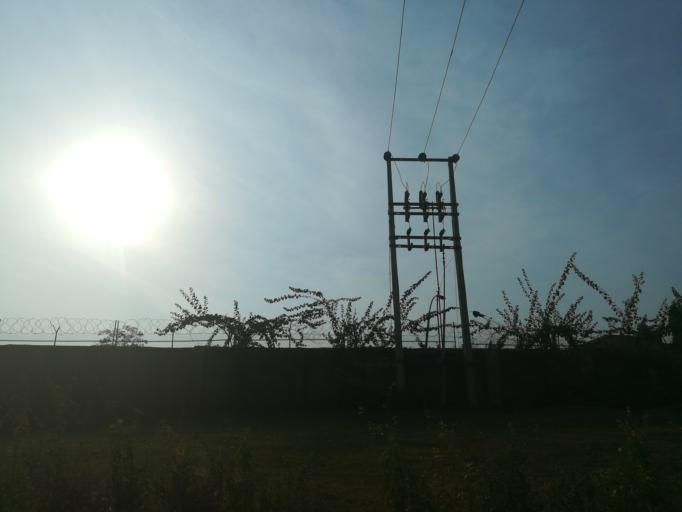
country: NG
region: Abuja Federal Capital Territory
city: Abuja
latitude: 9.0945
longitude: 7.3738
